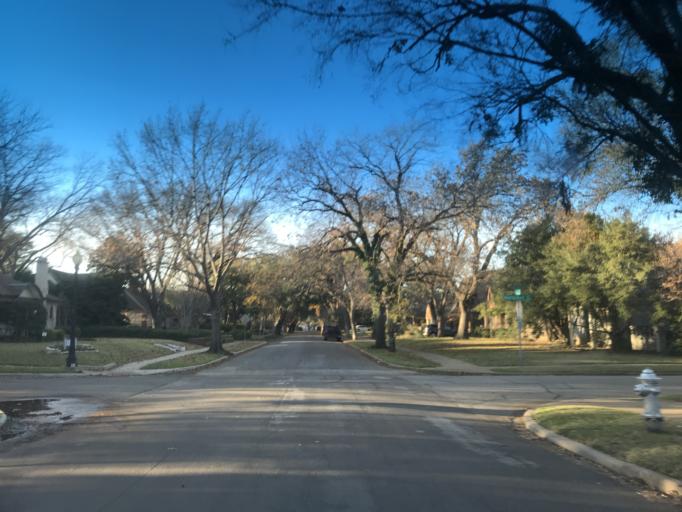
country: US
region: Texas
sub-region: Dallas County
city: Highland Park
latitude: 32.8162
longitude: -96.8142
